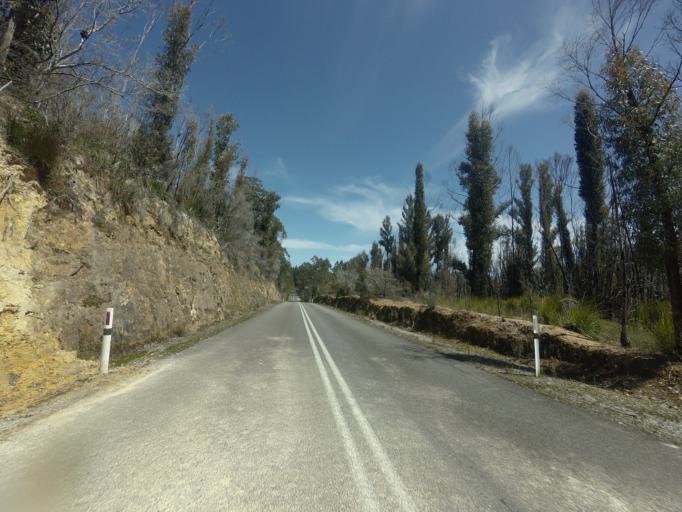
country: AU
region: Tasmania
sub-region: Huon Valley
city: Geeveston
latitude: -42.8391
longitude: 146.2596
